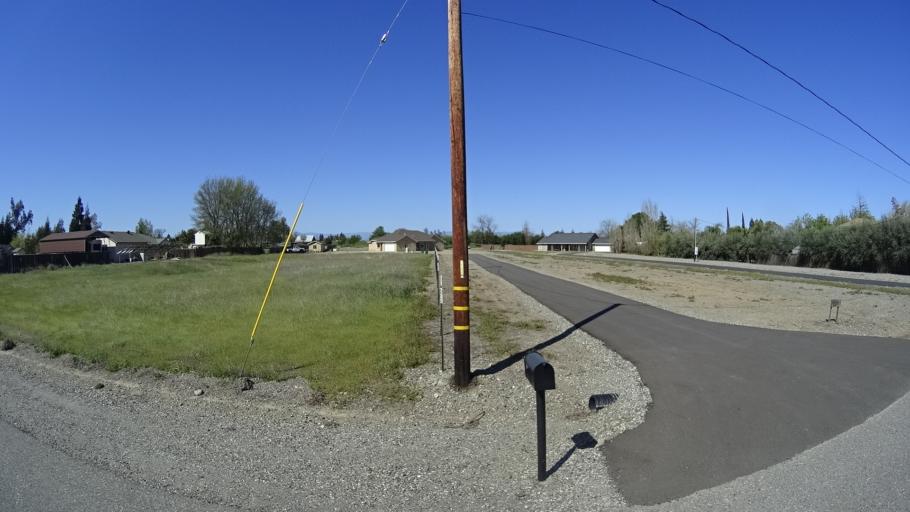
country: US
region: California
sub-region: Glenn County
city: Orland
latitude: 39.7461
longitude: -122.2133
